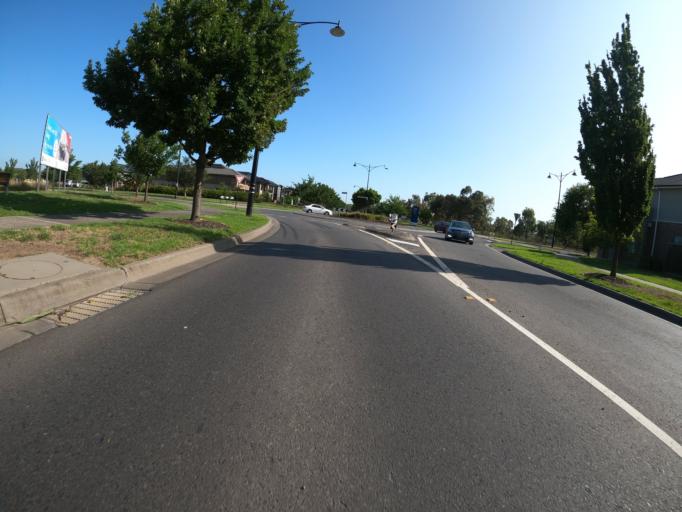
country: AU
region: Victoria
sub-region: Hume
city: Roxburgh Park
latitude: -37.5885
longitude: 144.9060
